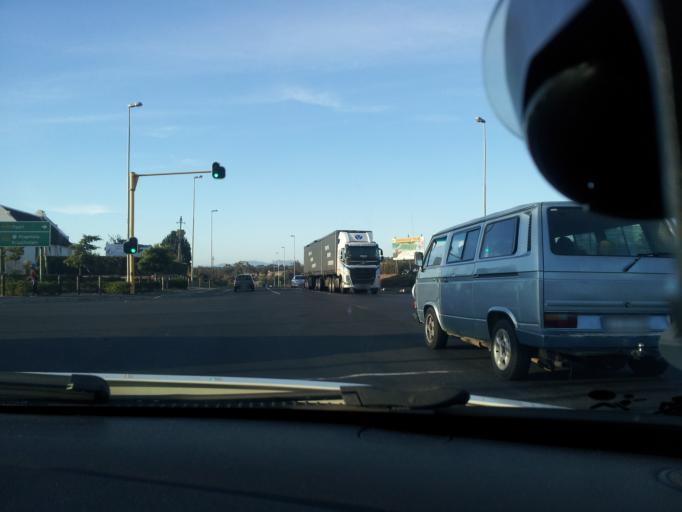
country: ZA
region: Western Cape
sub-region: Cape Winelands District Municipality
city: Paarl
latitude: -33.8040
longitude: 18.8725
